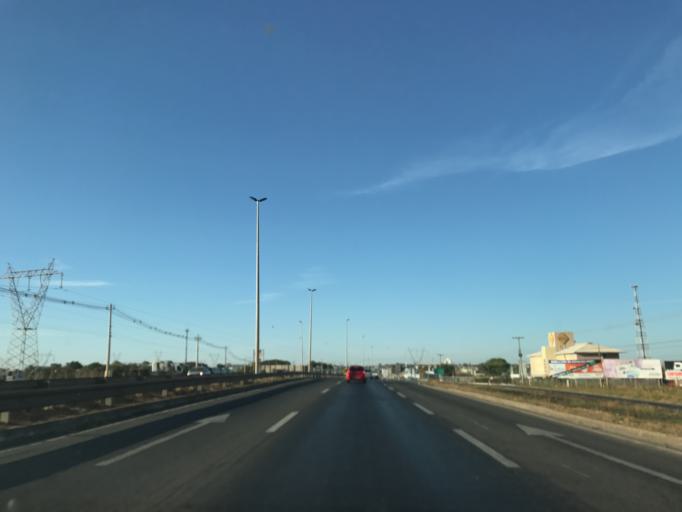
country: BR
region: Goias
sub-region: Aparecida De Goiania
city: Aparecida de Goiania
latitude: -16.7978
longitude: -49.2386
